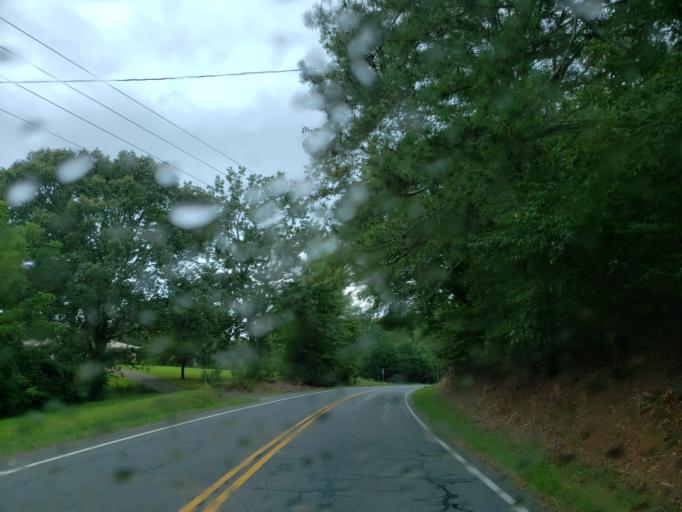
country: US
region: Georgia
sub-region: Gilmer County
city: Ellijay
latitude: 34.6236
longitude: -84.5781
